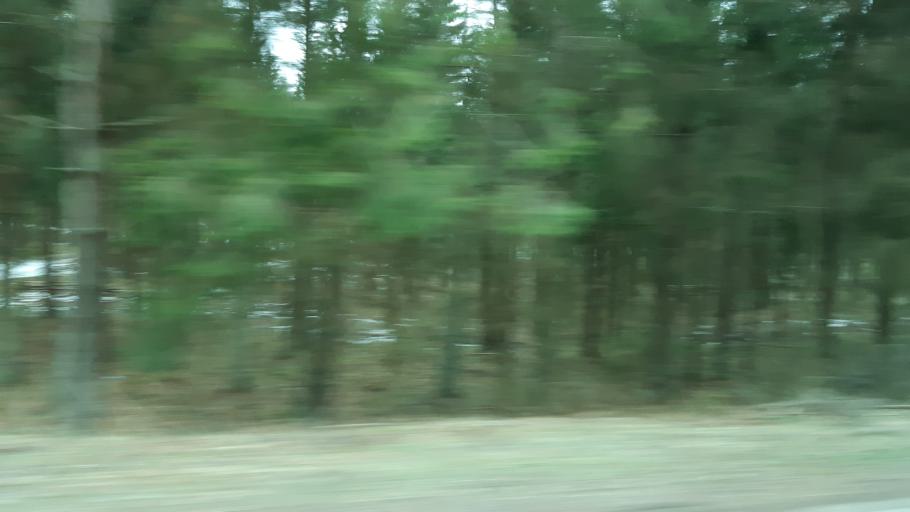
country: PL
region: Podlasie
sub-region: Suwalki
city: Suwalki
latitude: 54.2956
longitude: 22.9590
